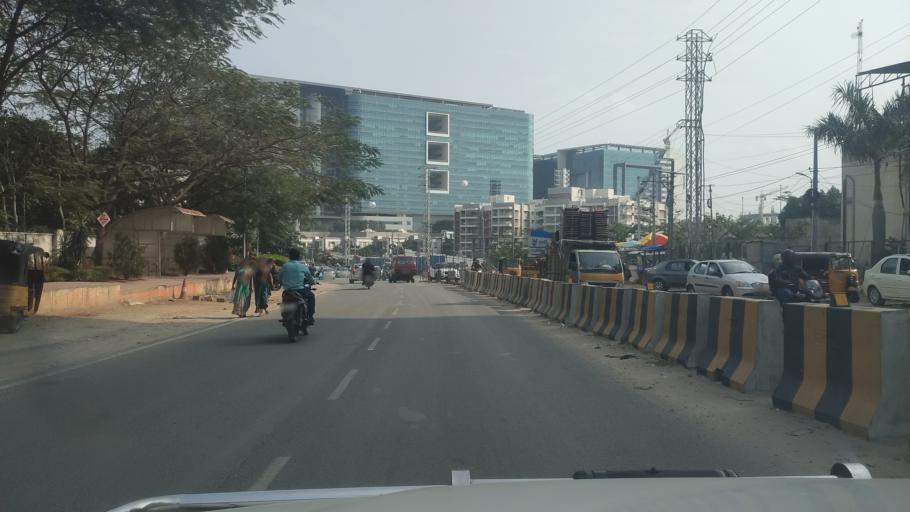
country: IN
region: Telangana
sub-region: Rangareddi
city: Kukatpalli
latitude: 17.4446
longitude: 78.3668
